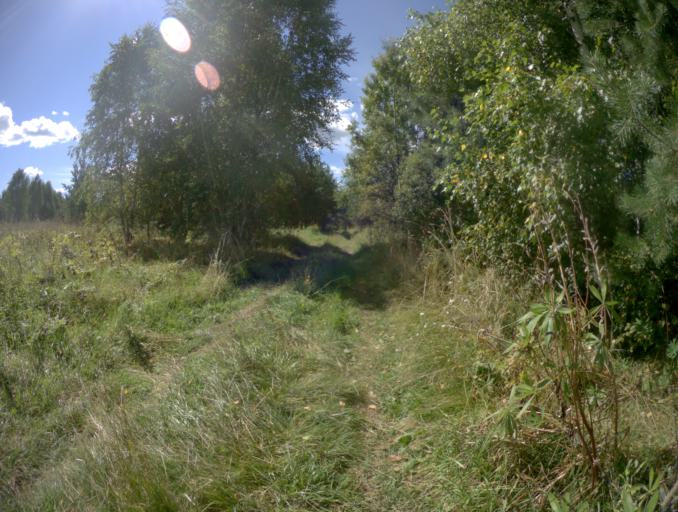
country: RU
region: Vladimir
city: Krasnaya Gorbatka
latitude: 55.8747
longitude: 41.8568
